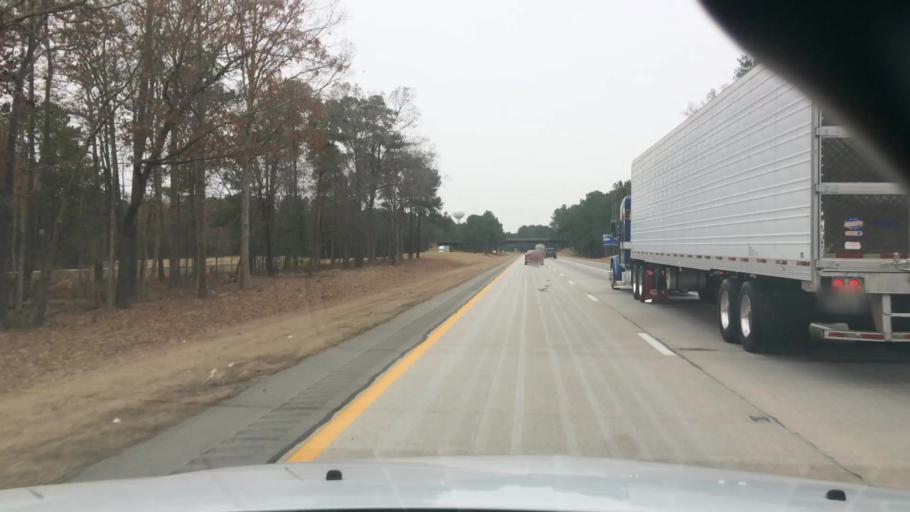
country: US
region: North Carolina
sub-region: Nash County
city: Nashville
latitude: 35.8762
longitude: -77.9510
